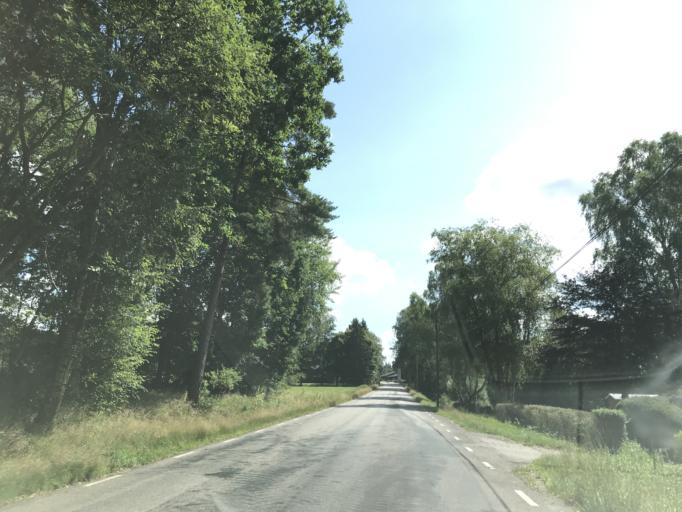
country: SE
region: Halland
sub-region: Laholms Kommun
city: Knared
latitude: 56.5207
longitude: 13.3366
